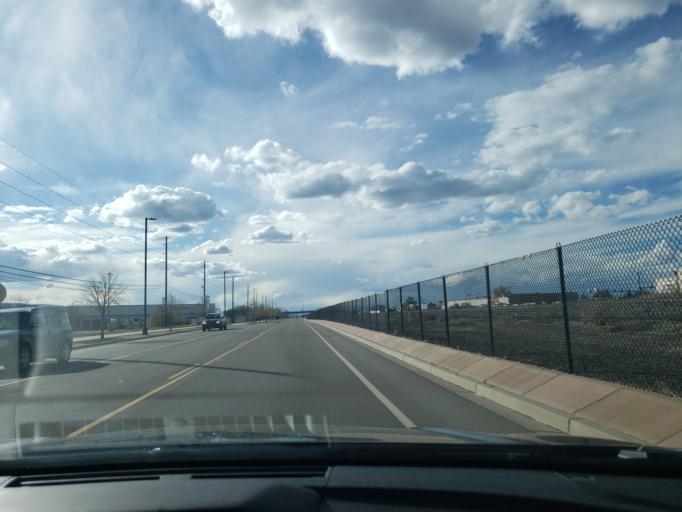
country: US
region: Colorado
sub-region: Mesa County
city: Redlands
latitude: 39.0863
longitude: -108.5999
